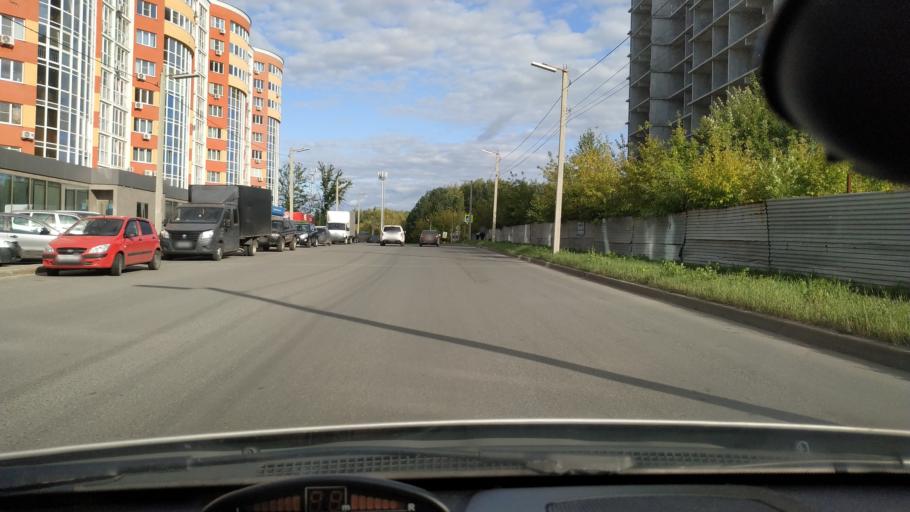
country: RU
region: Rjazan
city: Ryazan'
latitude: 54.6042
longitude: 39.7403
